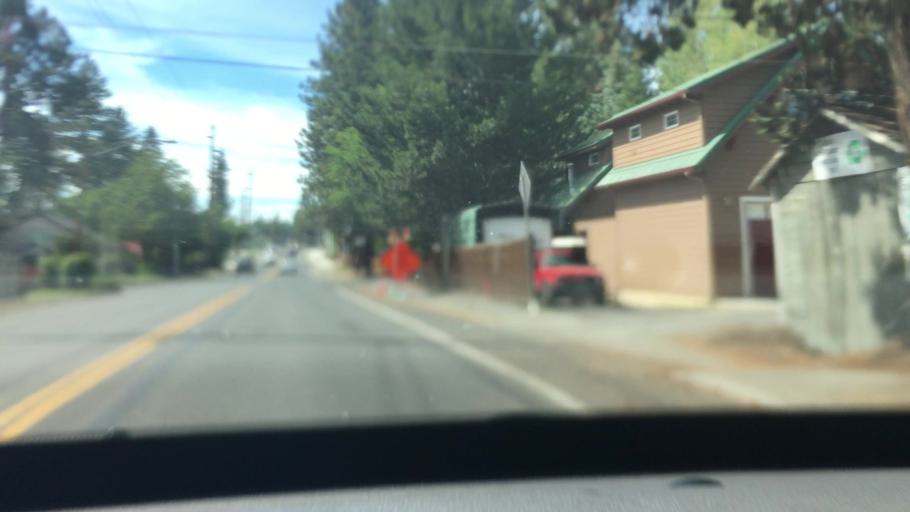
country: US
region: Oregon
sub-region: Deschutes County
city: Bend
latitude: 44.0532
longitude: -121.3319
